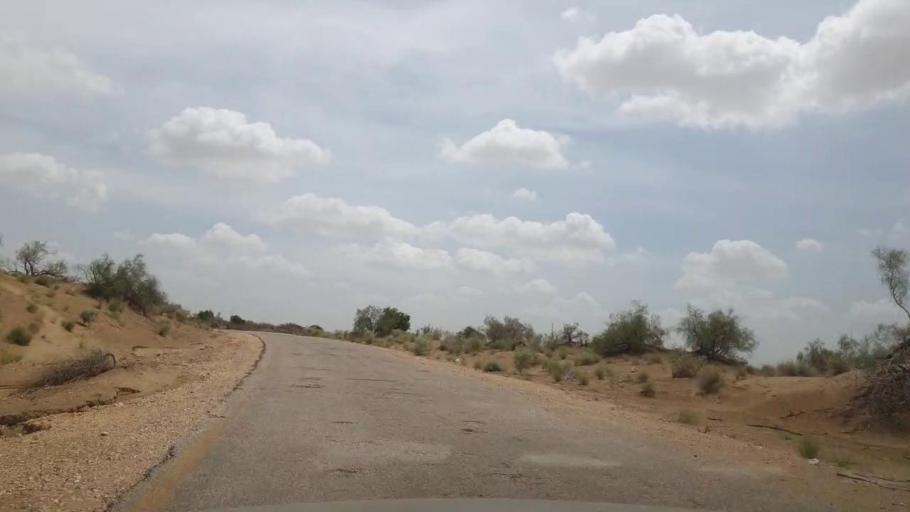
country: PK
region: Sindh
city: Kot Diji
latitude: 27.1447
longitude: 69.2247
